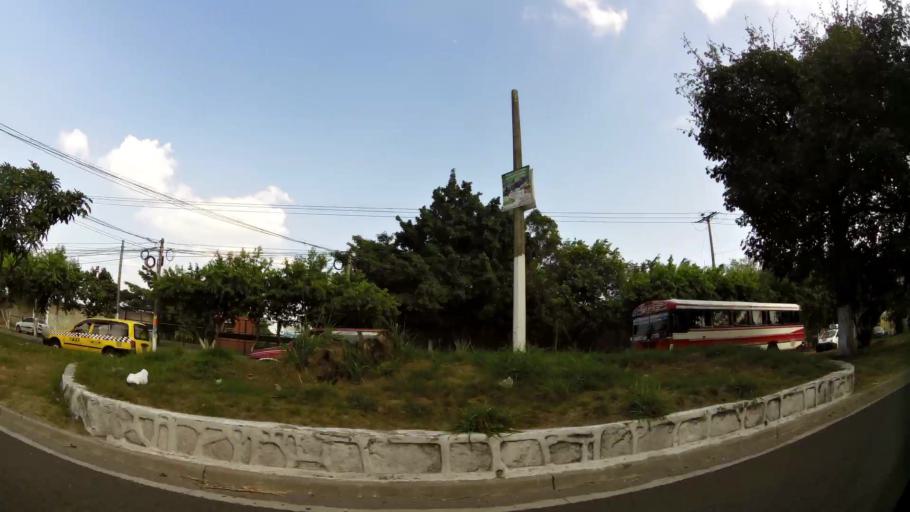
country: SV
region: San Salvador
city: Soyapango
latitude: 13.7169
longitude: -89.1413
